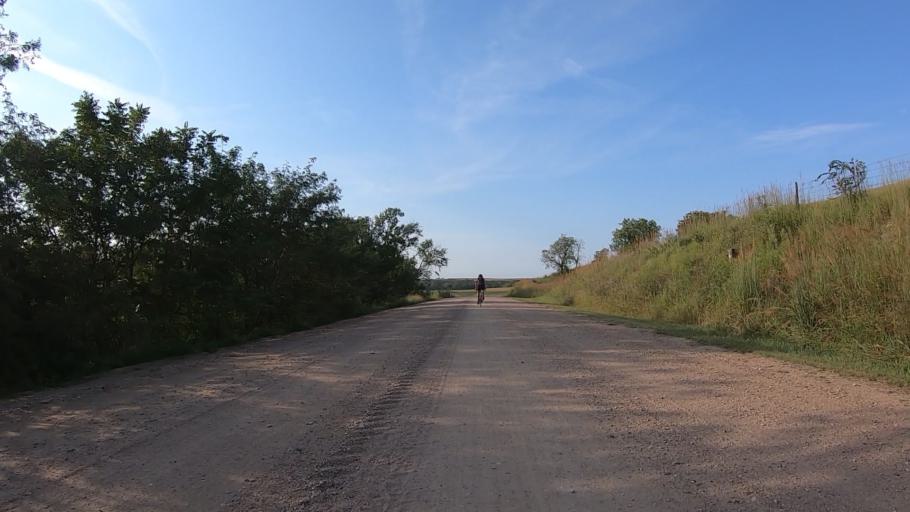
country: US
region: Kansas
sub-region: Marshall County
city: Blue Rapids
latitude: 39.6832
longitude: -96.7792
